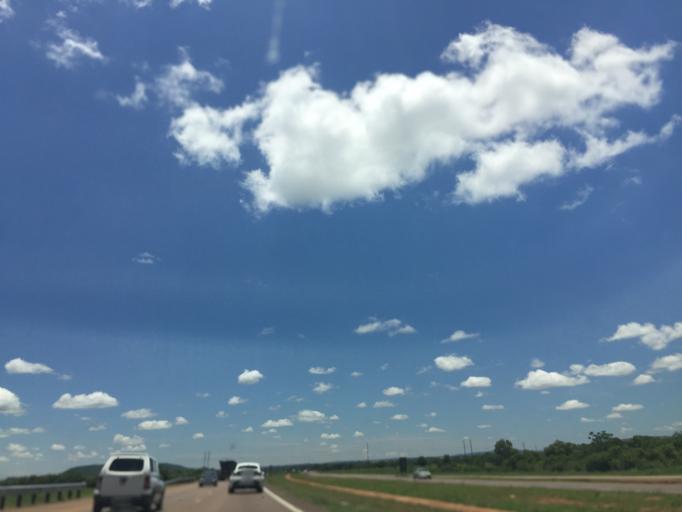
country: ZA
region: Gauteng
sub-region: City of Tshwane Metropolitan Municipality
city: Pretoria
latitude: -25.6466
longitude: 28.1522
